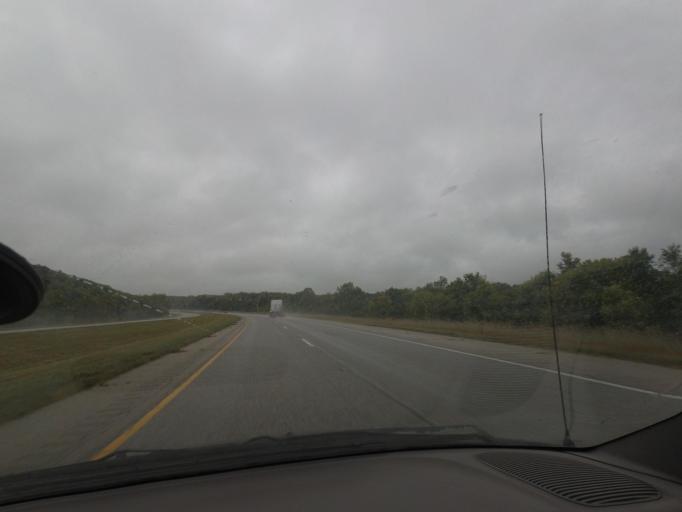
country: US
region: Illinois
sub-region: Pike County
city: Barry
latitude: 39.7144
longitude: -91.1052
